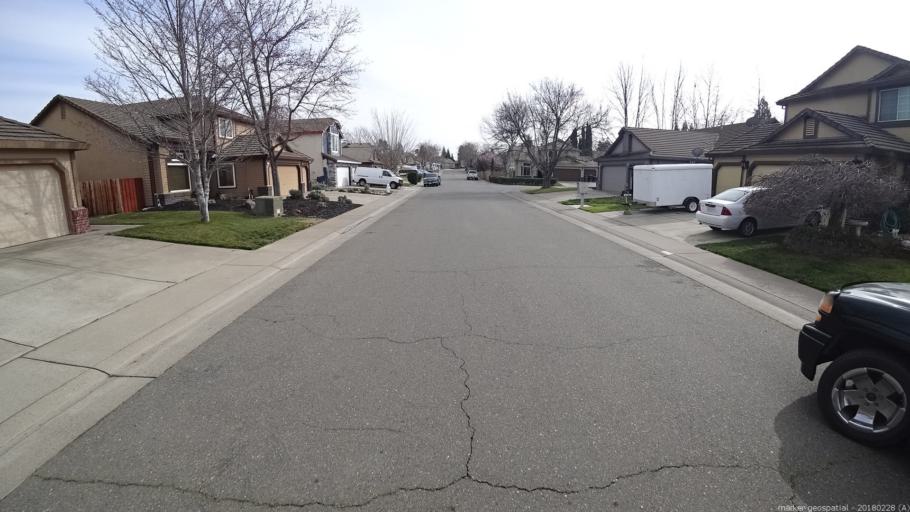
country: US
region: California
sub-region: Sacramento County
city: Antelope
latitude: 38.7246
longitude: -121.3403
